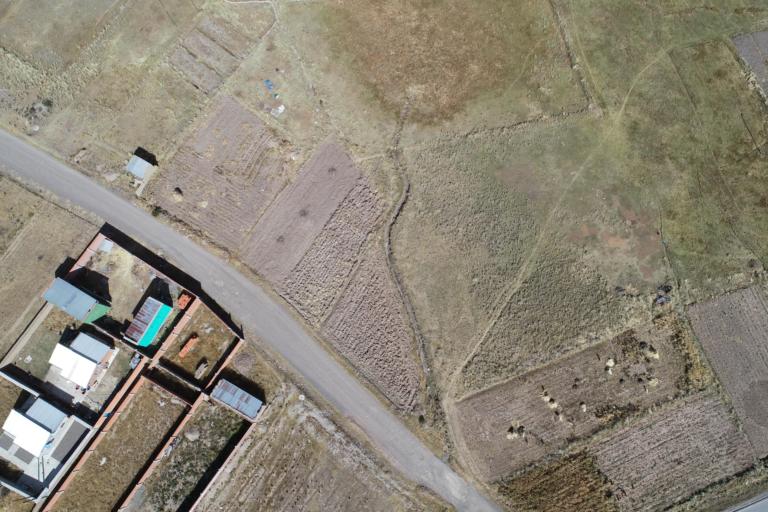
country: BO
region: La Paz
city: Achacachi
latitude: -15.8955
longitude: -68.9097
